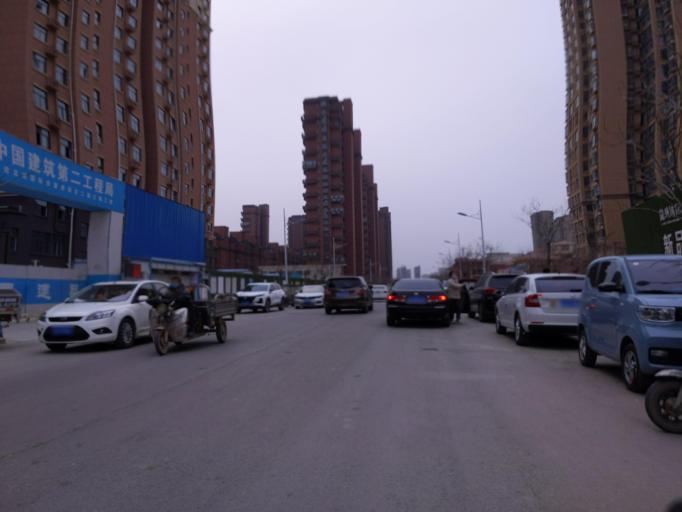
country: CN
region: Henan Sheng
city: Zhongyuanlu
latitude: 35.7429
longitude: 115.0722
